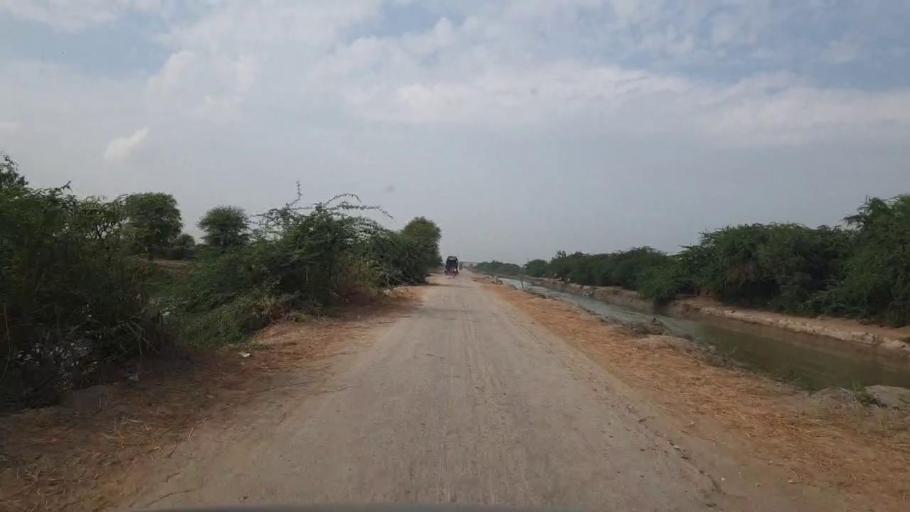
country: PK
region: Sindh
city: Kario
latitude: 24.6349
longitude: 68.5675
